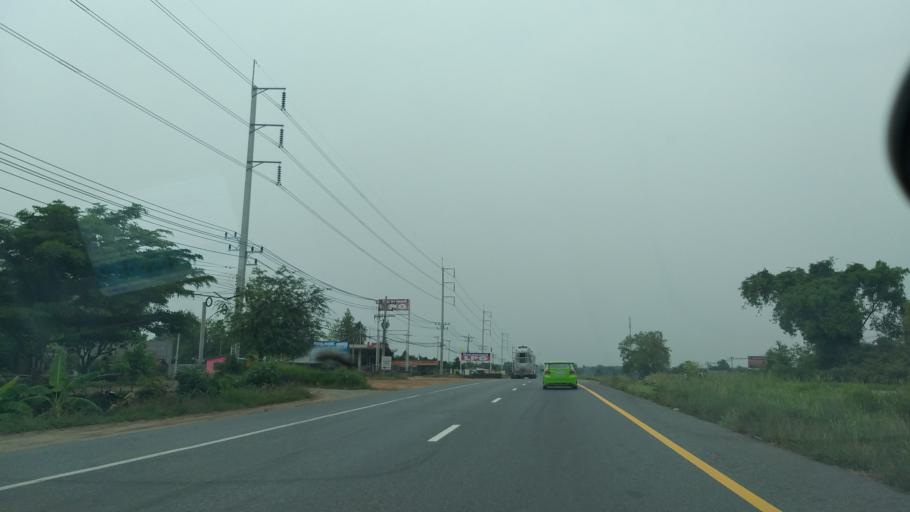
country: TH
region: Chon Buri
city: Ko Chan
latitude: 13.4350
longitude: 101.2830
